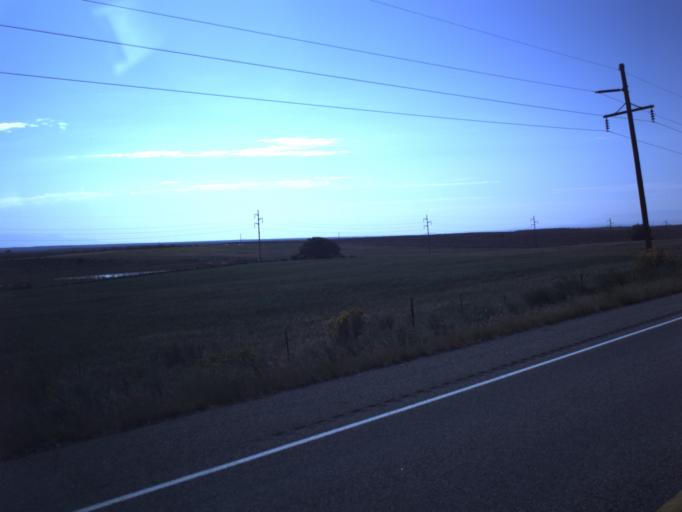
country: US
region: Utah
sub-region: San Juan County
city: Blanding
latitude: 37.5866
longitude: -109.4783
